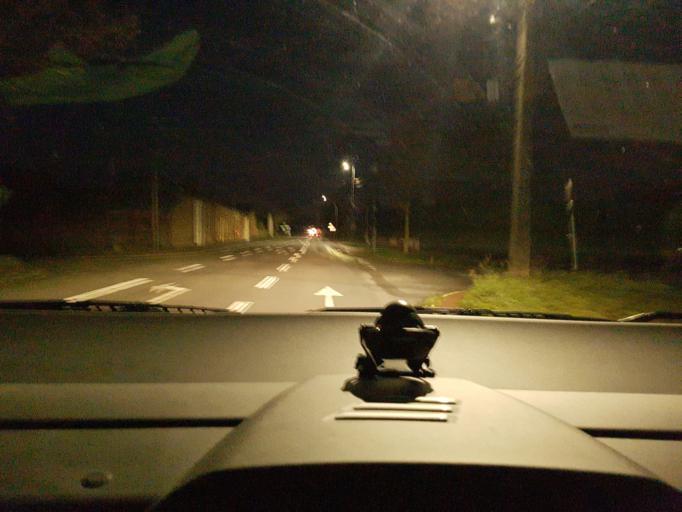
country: FR
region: Nord-Pas-de-Calais
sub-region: Departement du Pas-de-Calais
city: Neuville-Saint-Vaast
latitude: 50.3590
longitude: 2.7469
